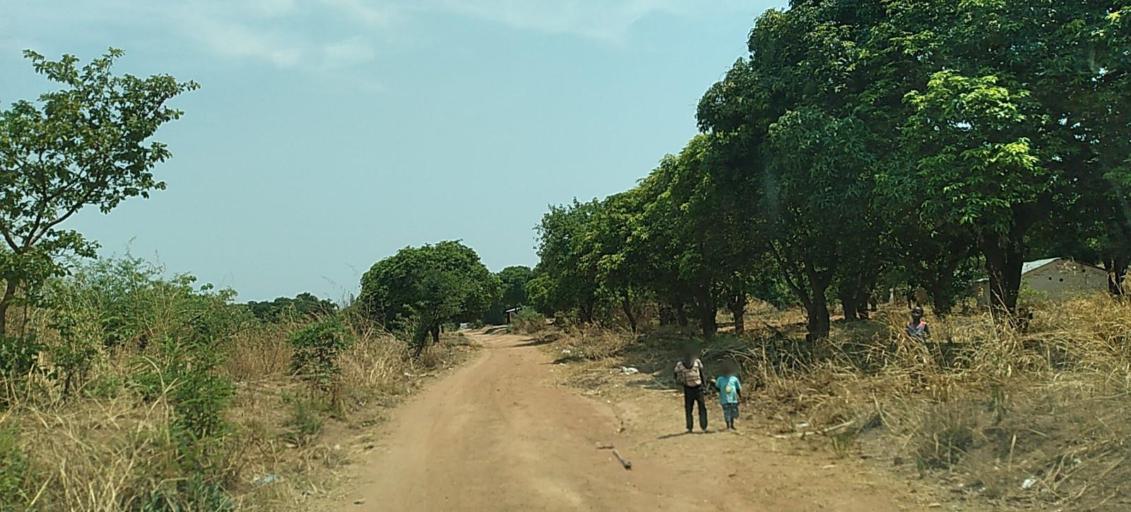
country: ZM
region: Copperbelt
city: Ndola
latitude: -13.0763
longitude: 28.7469
